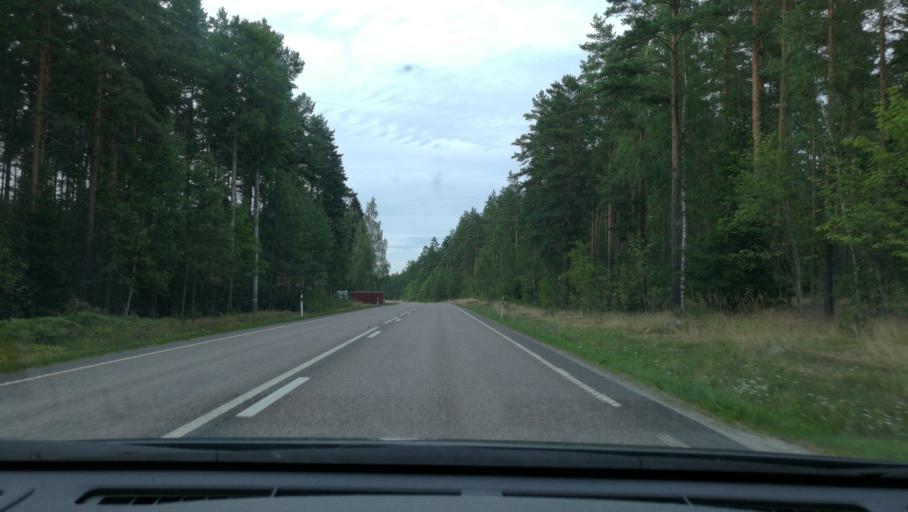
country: SE
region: Vaestmanland
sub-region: Kungsors Kommun
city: Kungsoer
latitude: 59.2192
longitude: 16.0997
